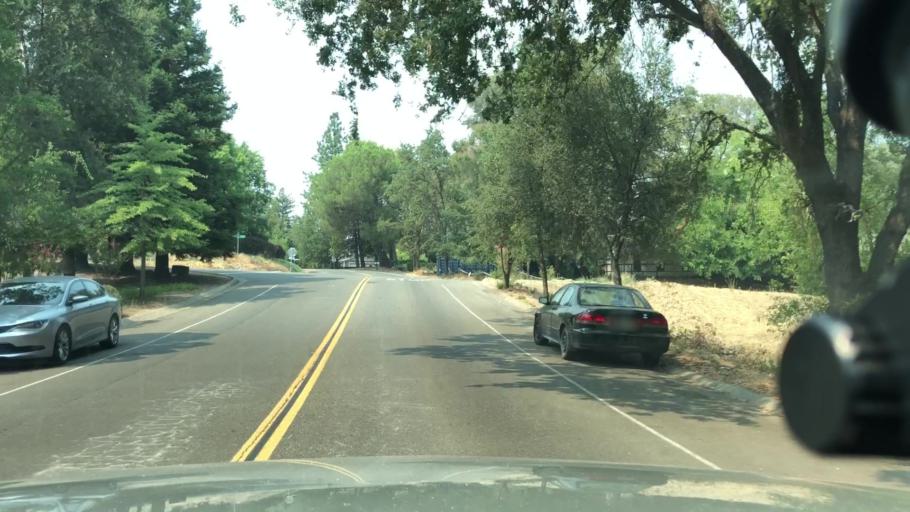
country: US
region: California
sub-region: El Dorado County
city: Cameron Park
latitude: 38.6606
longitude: -121.0003
